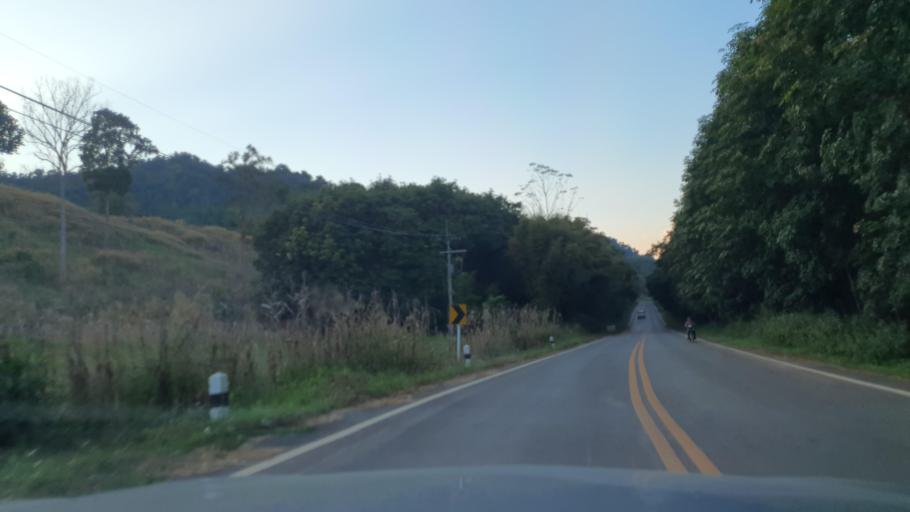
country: TH
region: Phayao
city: Chiang Muan
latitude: 18.8997
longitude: 100.1273
